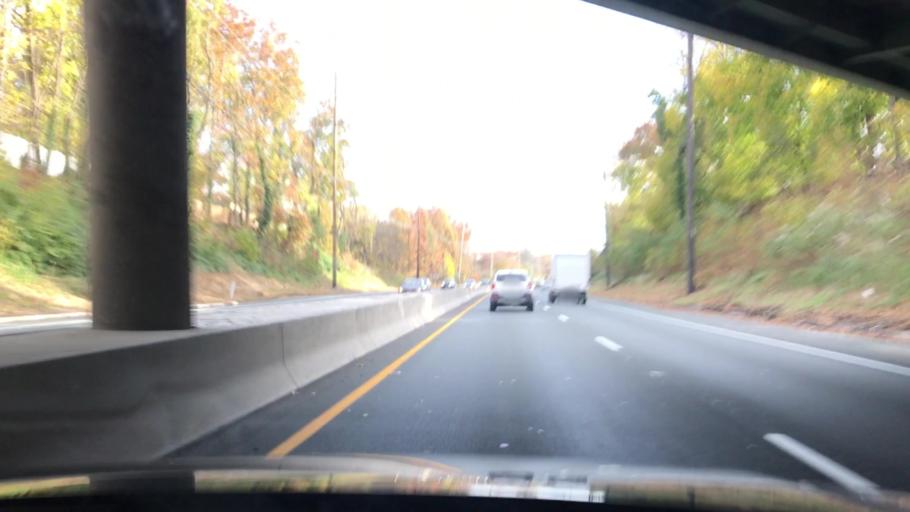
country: US
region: New Jersey
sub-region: Bergen County
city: Glen Rock
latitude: 40.9585
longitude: -74.1436
